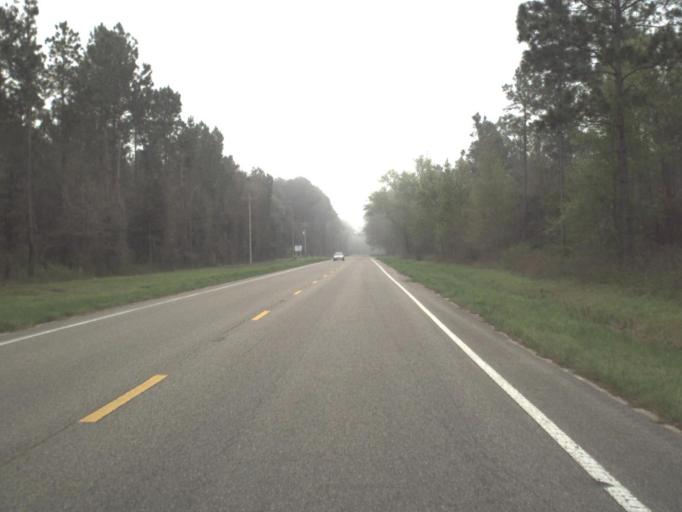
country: US
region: Florida
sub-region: Gadsden County
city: Gretna
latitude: 30.5279
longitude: -84.6878
